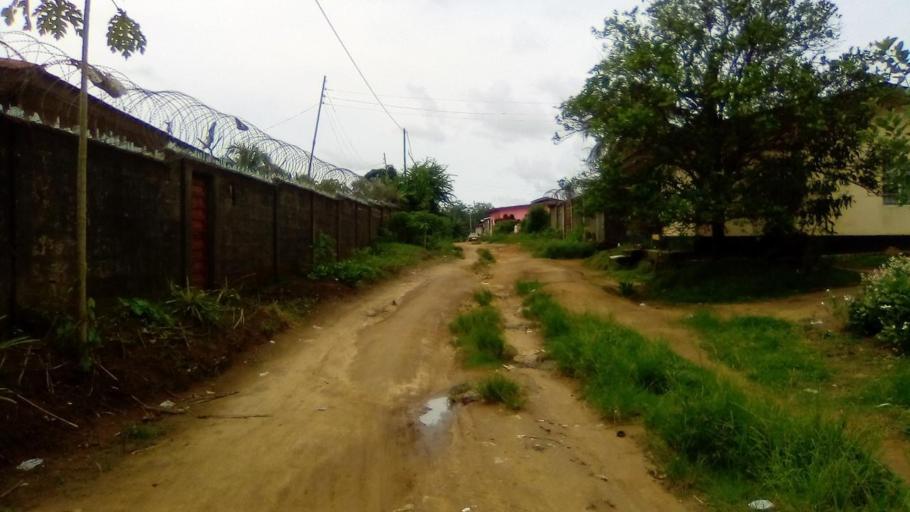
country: SL
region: Southern Province
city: Bo
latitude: 7.9508
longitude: -11.7524
